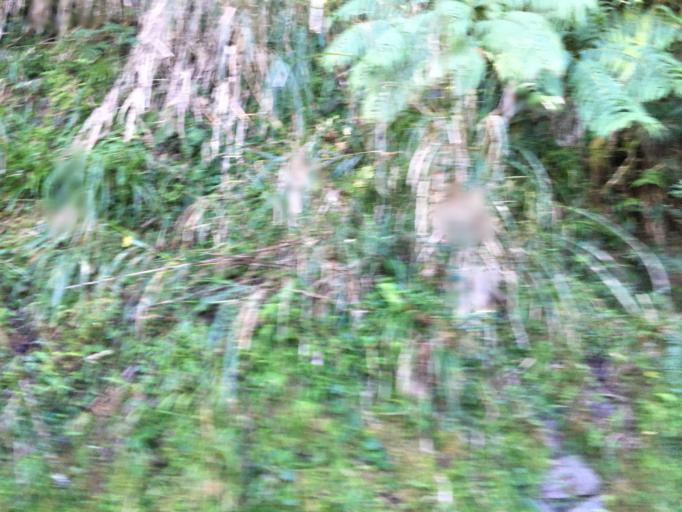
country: TW
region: Taiwan
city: Daxi
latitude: 24.5684
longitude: 121.4130
